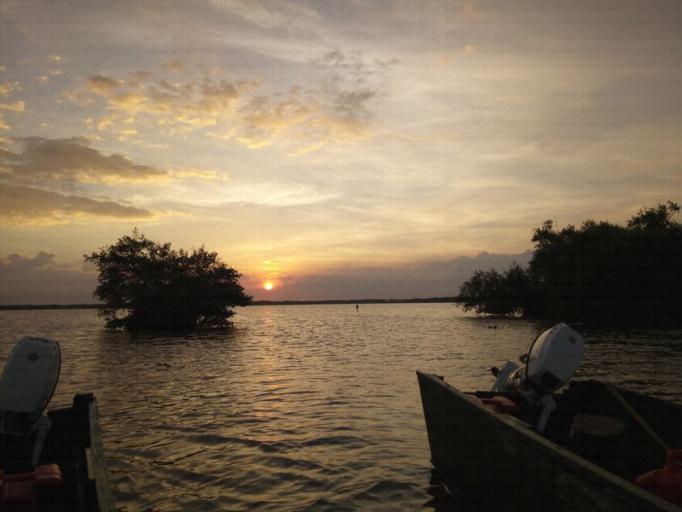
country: SR
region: Nickerie
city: Nieuw Nickerie
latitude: 5.9630
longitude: -56.8511
